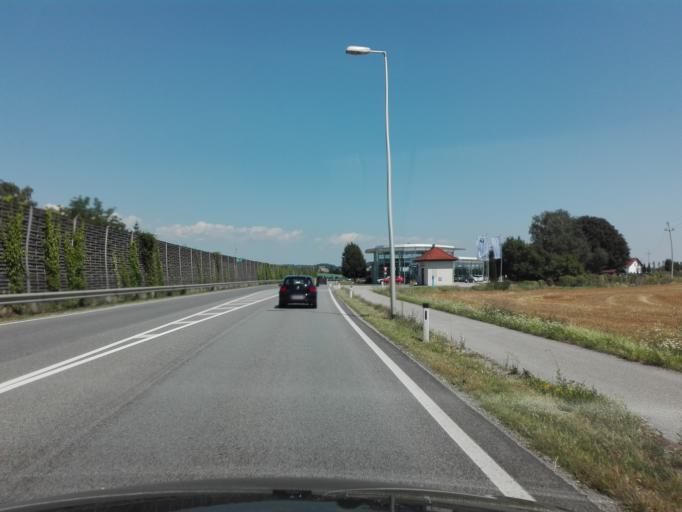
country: AT
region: Lower Austria
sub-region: Politischer Bezirk Amstetten
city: Ennsdorf
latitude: 48.2463
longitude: 14.5542
